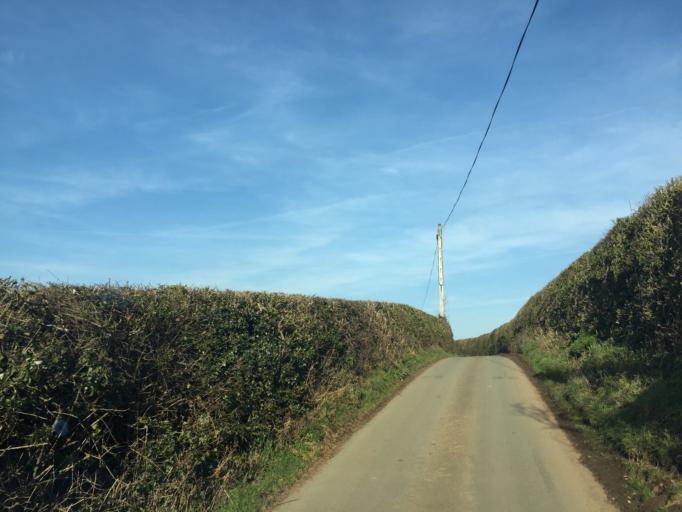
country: GB
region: England
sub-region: Shropshire
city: Bridgnorth
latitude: 52.5357
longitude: -2.4770
